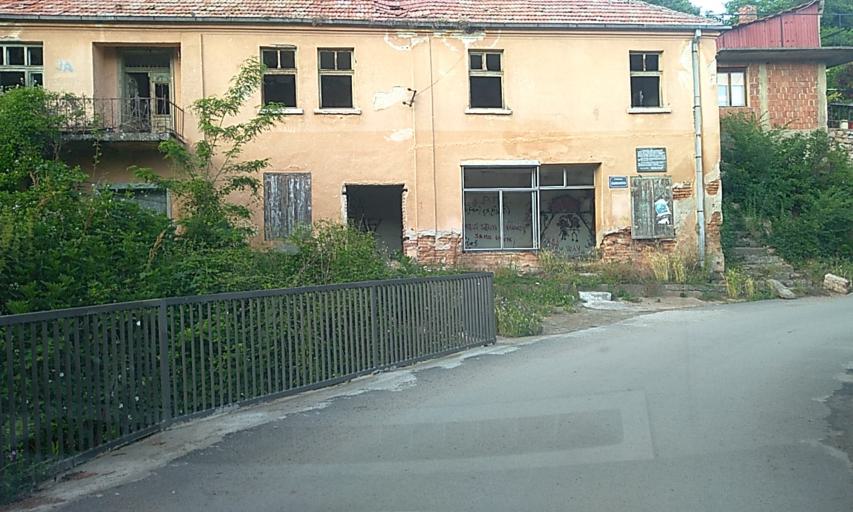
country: RS
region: Central Serbia
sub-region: Nisavski Okrug
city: Nis
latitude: 43.3693
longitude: 21.9672
